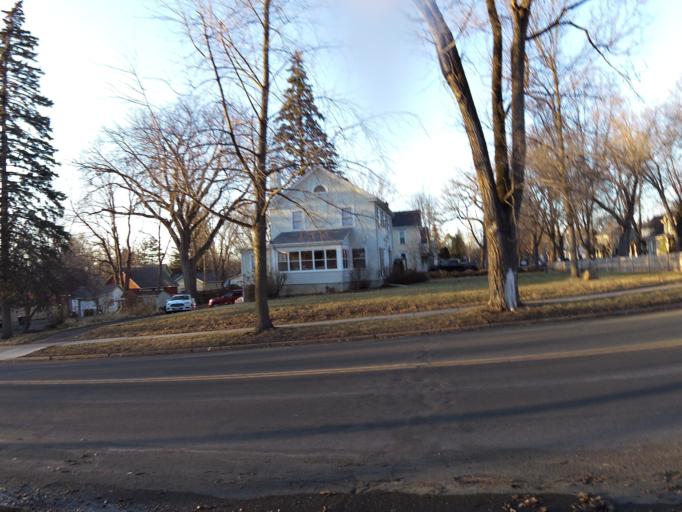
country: US
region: Wisconsin
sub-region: Saint Croix County
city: Hudson
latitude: 44.9825
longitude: -92.7559
